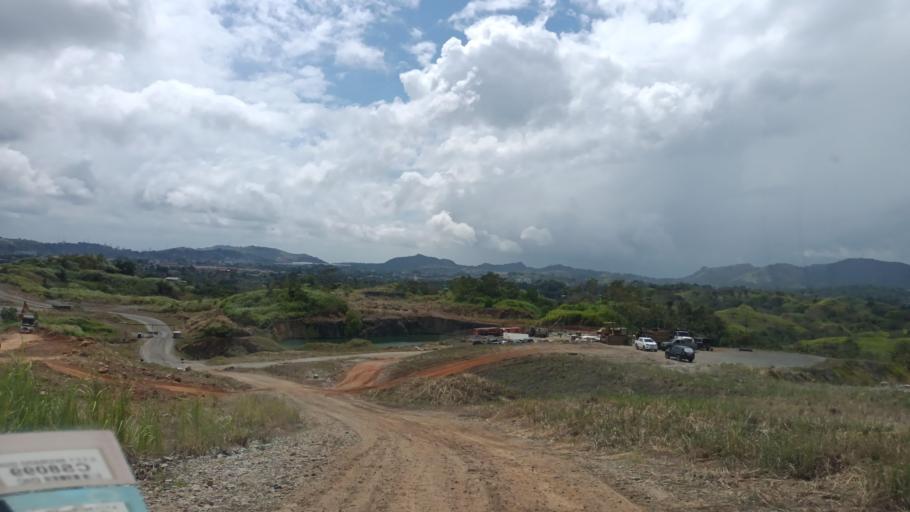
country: PA
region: Panama
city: Las Cumbres
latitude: 9.1100
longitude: -79.4992
